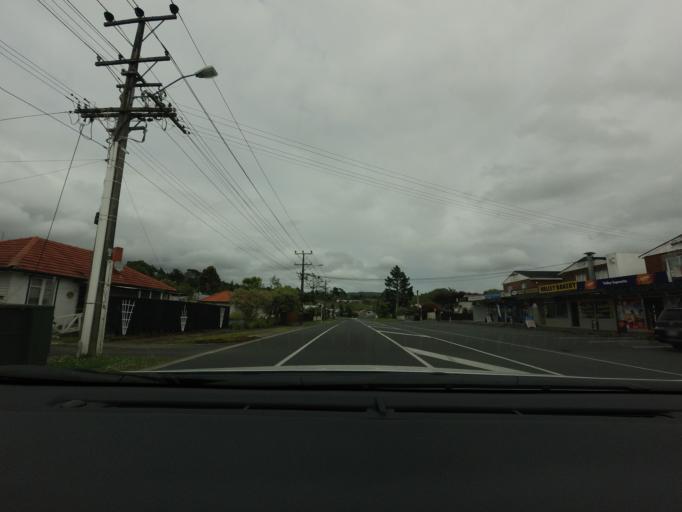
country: NZ
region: Auckland
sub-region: Auckland
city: Waitakere
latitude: -36.8973
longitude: 174.6141
